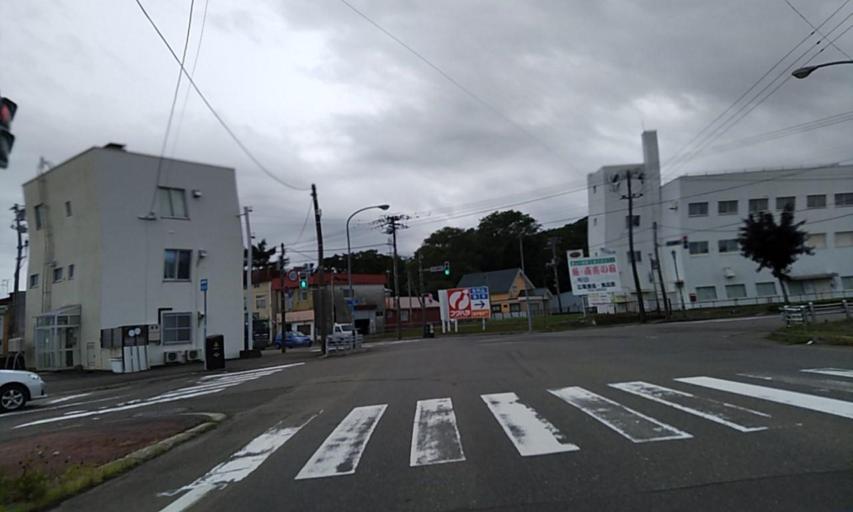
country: JP
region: Hokkaido
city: Obihiro
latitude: 42.2935
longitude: 143.3123
